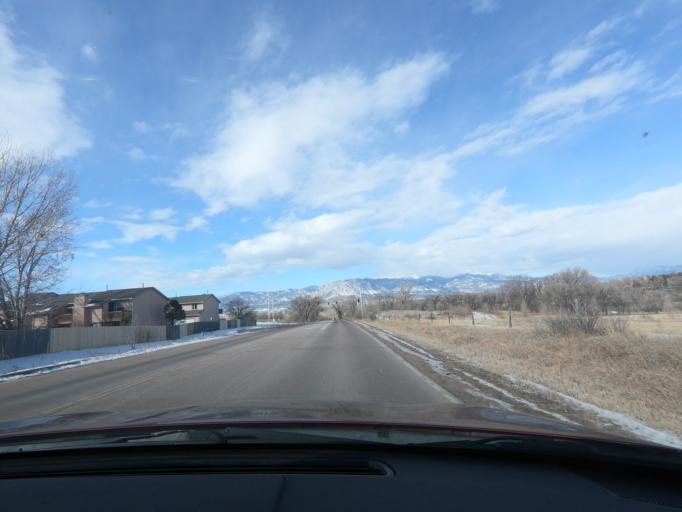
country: US
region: Colorado
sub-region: El Paso County
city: Security-Widefield
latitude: 38.7375
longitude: -104.7039
